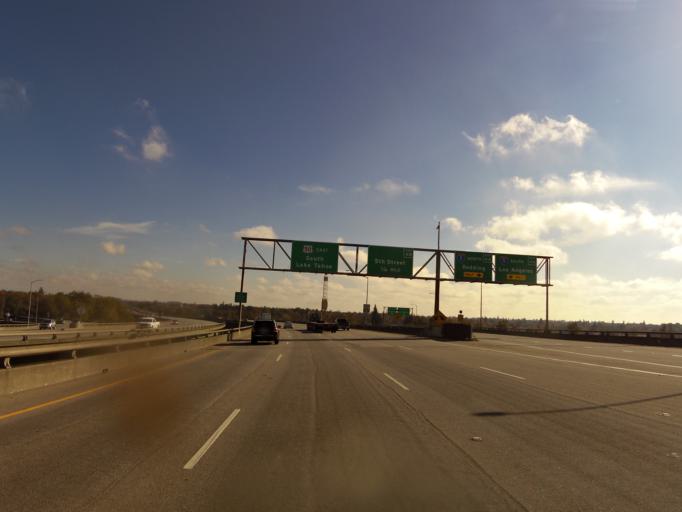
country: US
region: California
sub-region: Yolo County
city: West Sacramento
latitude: 38.5704
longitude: -121.5143
